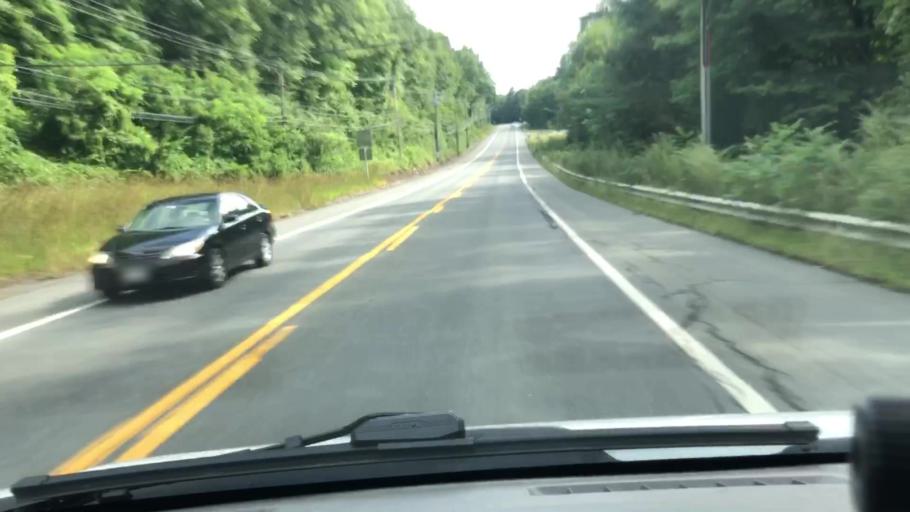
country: US
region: Massachusetts
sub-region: Franklin County
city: Shelburne Falls
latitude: 42.5995
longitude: -72.7299
